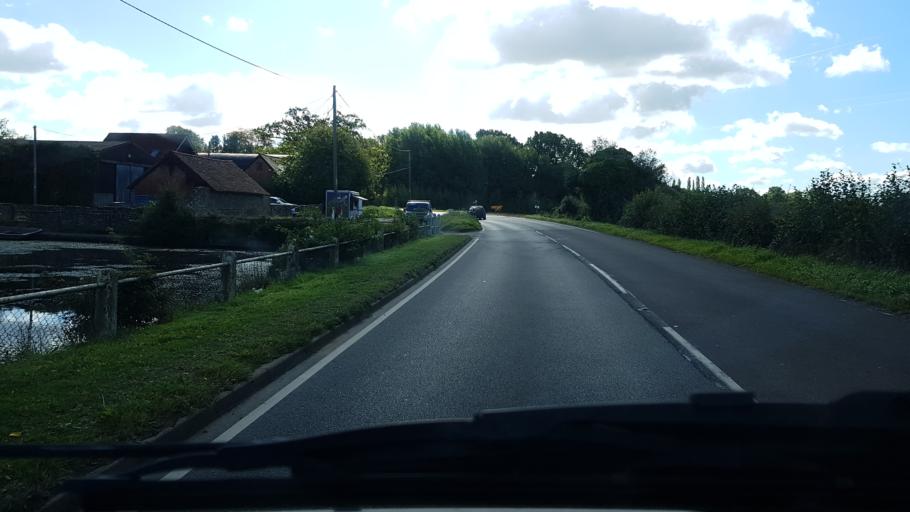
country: GB
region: England
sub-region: West Sussex
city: Rudgwick
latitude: 51.0636
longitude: -0.5158
